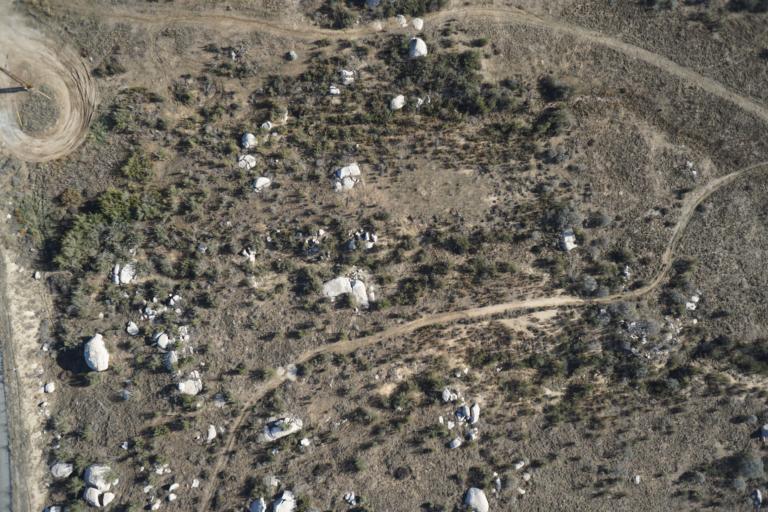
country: US
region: California
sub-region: Riverside County
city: East Hemet
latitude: 33.6184
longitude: -116.9002
